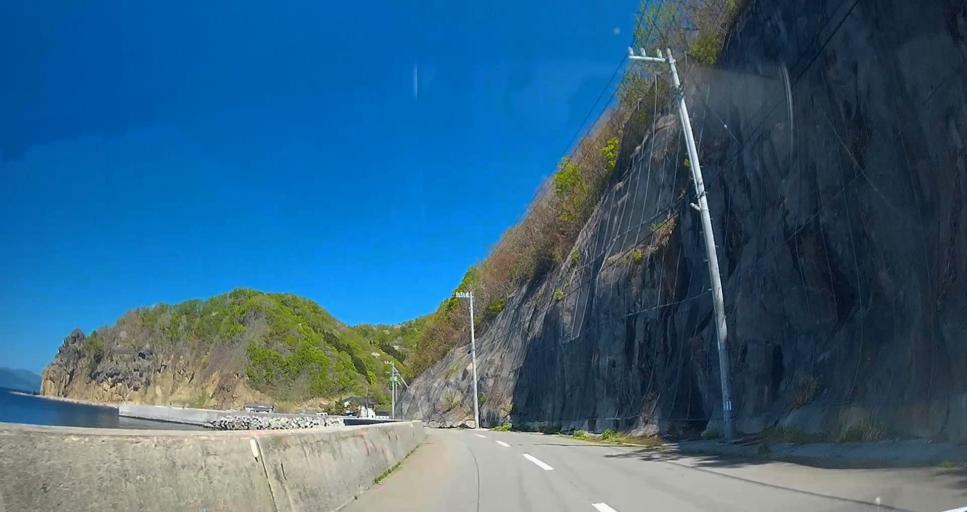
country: JP
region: Aomori
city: Aomori Shi
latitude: 41.1395
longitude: 140.7747
